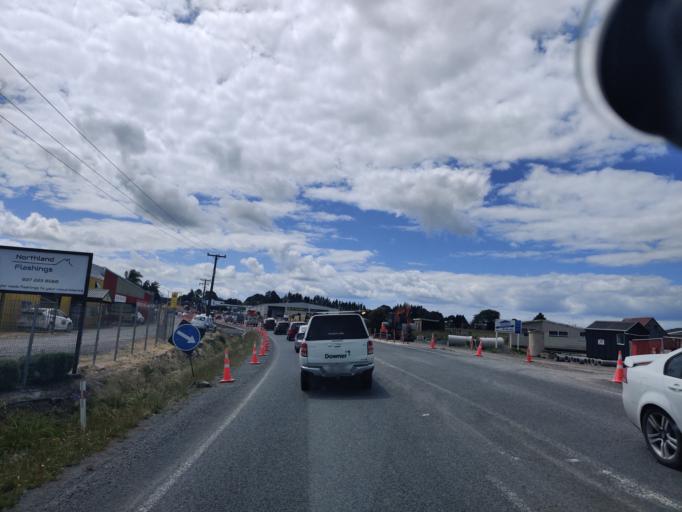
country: NZ
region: Northland
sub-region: Far North District
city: Kerikeri
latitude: -35.2088
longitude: 173.9199
